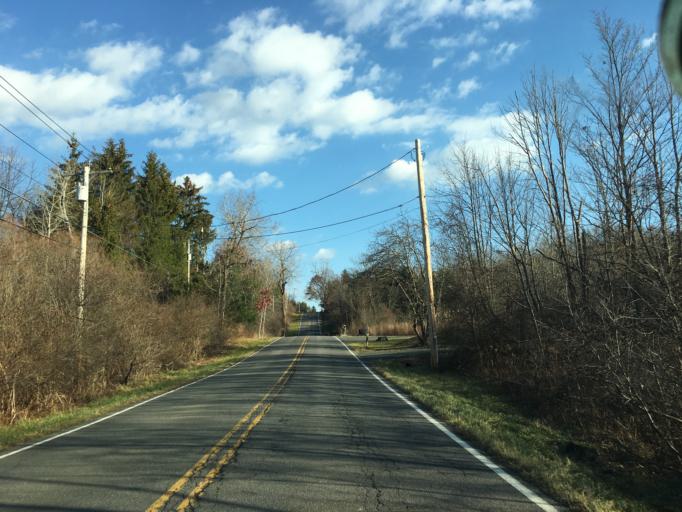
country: US
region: New York
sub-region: Rensselaer County
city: East Greenbush
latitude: 42.6318
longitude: -73.6840
